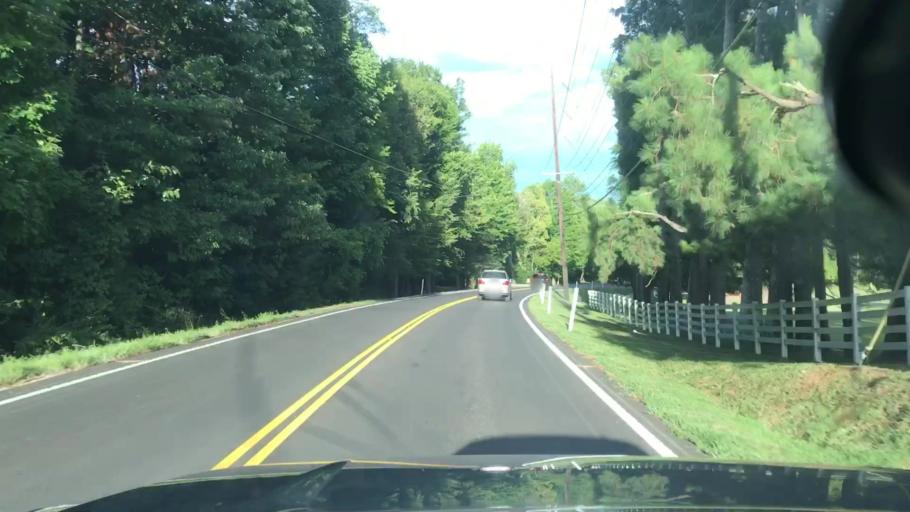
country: US
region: Tennessee
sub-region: Davidson County
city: Forest Hills
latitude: 36.0428
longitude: -86.8288
